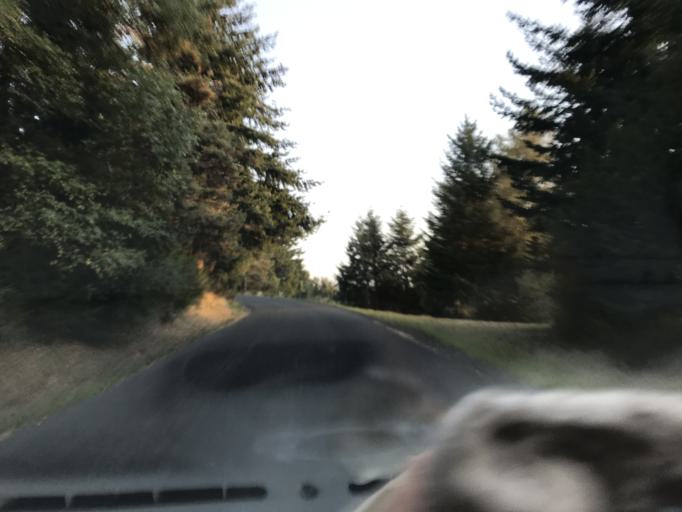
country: FR
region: Rhone-Alpes
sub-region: Departement de l'Ardeche
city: Saint-Agreve
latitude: 45.0137
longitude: 4.3926
